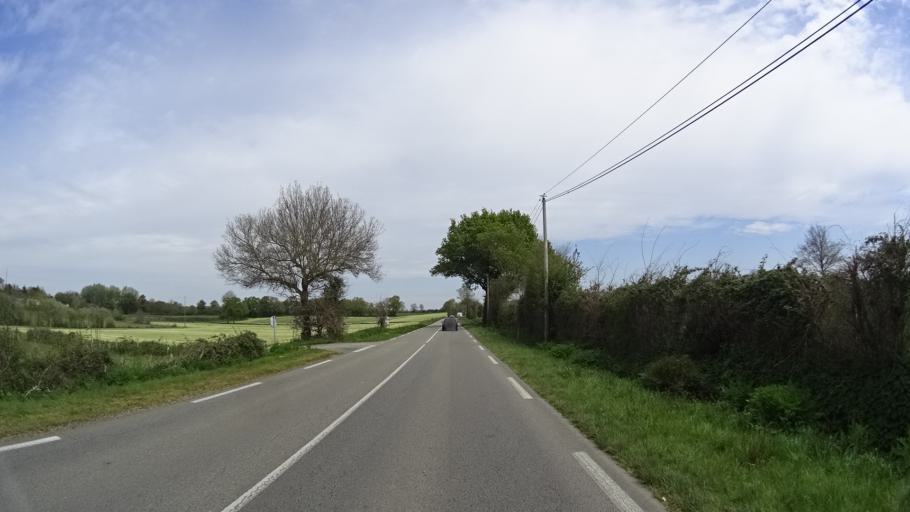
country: FR
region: Pays de la Loire
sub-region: Departement de la Loire-Atlantique
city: Sainte-Pazanne
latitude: 47.1116
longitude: -1.7804
